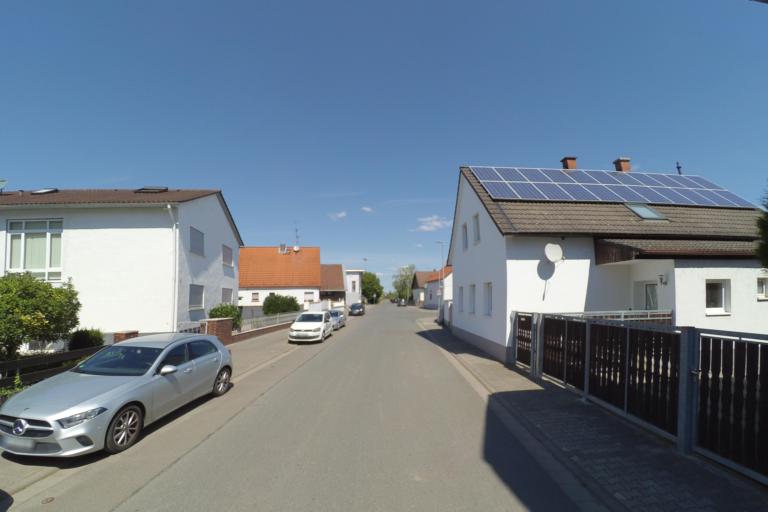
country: DE
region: Hesse
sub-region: Regierungsbezirk Darmstadt
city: Biblis
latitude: 49.6863
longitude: 8.4079
